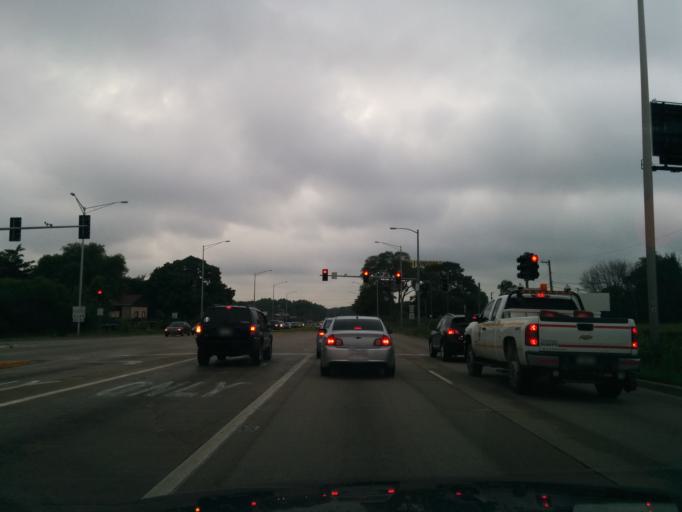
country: US
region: Illinois
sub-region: DuPage County
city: Addison
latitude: 41.9250
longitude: -87.9681
